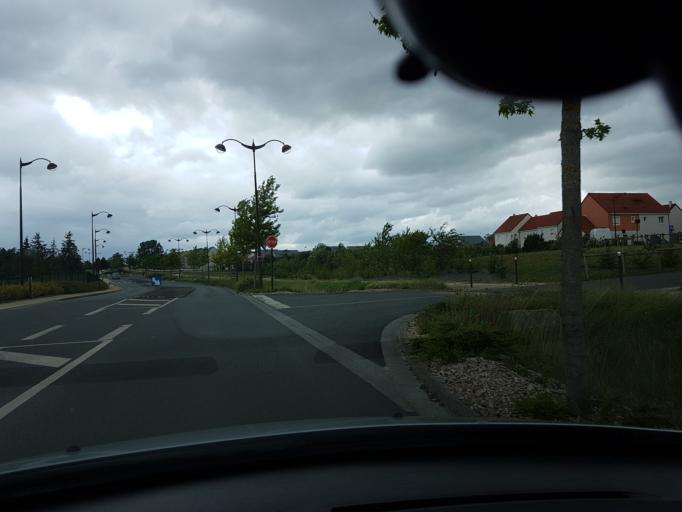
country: FR
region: Centre
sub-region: Departement du Cher
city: Bourges
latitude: 47.1071
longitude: 2.4222
